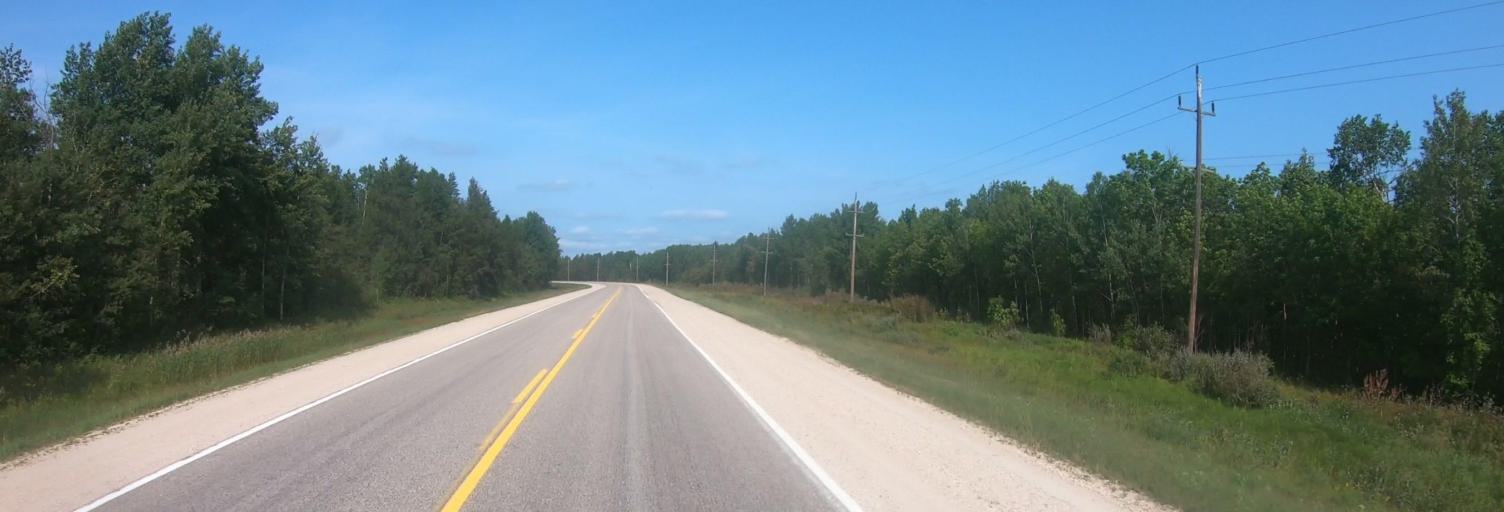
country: CA
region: Manitoba
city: La Broquerie
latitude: 49.1724
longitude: -96.1588
